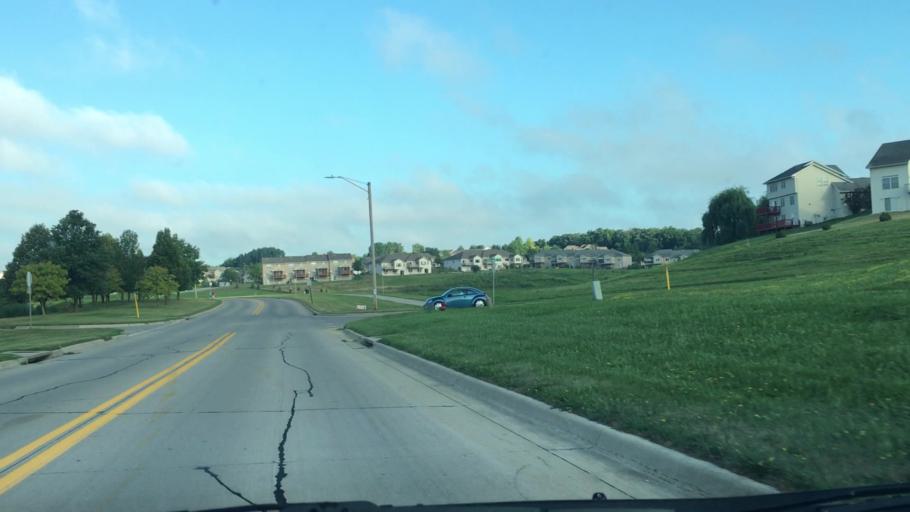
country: US
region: Iowa
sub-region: Johnson County
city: Coralville
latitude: 41.7020
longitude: -91.5552
